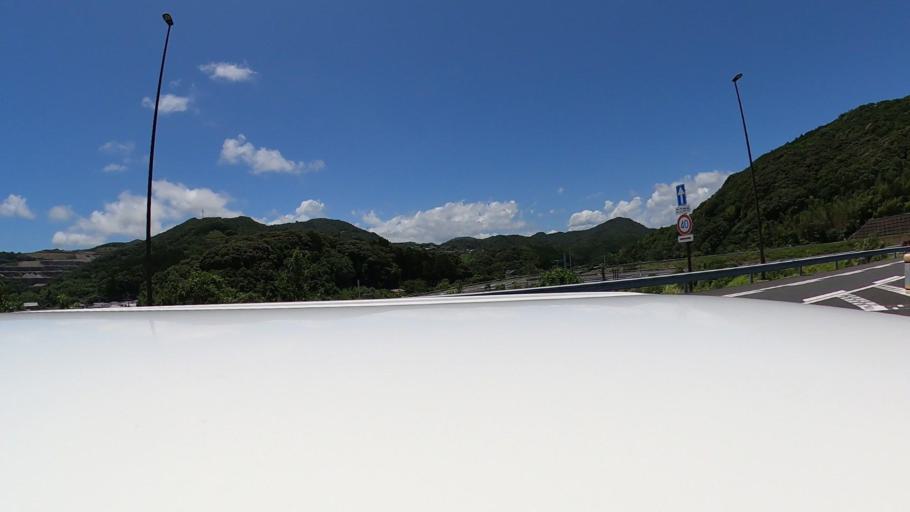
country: JP
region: Miyazaki
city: Nobeoka
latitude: 32.4003
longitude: 131.6169
